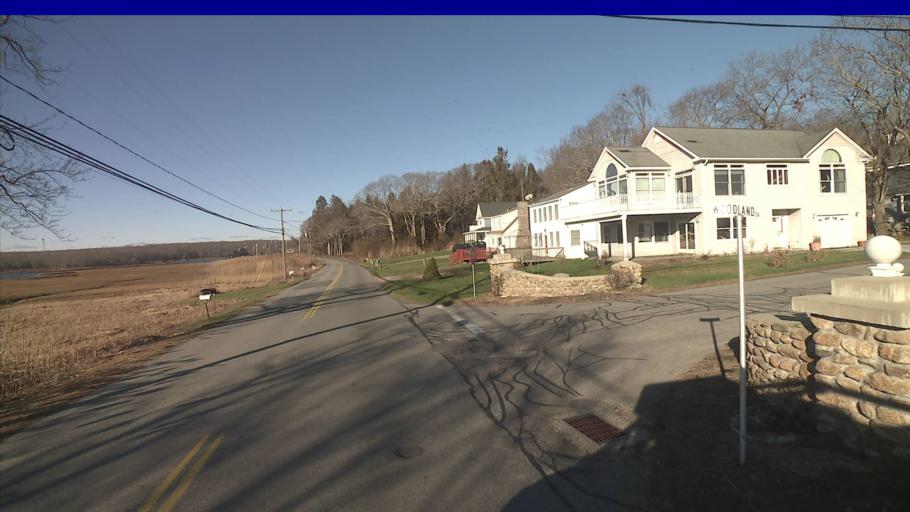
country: US
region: Connecticut
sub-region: New London County
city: Niantic
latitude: 41.3004
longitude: -72.2158
